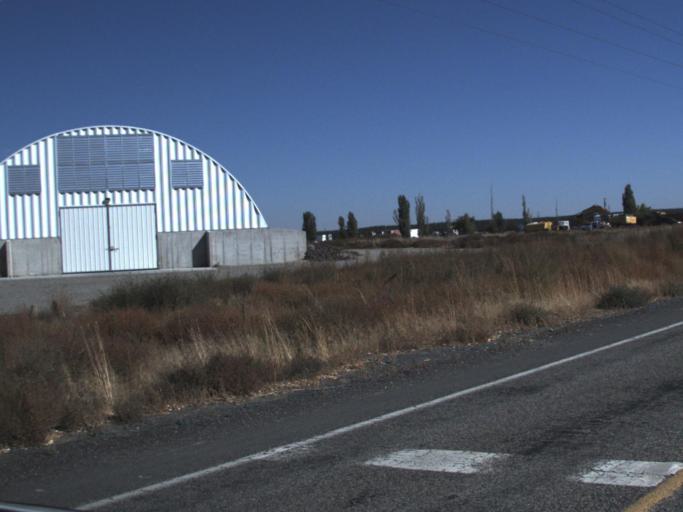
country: US
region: Washington
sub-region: Walla Walla County
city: Burbank
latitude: 46.2149
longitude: -118.9027
